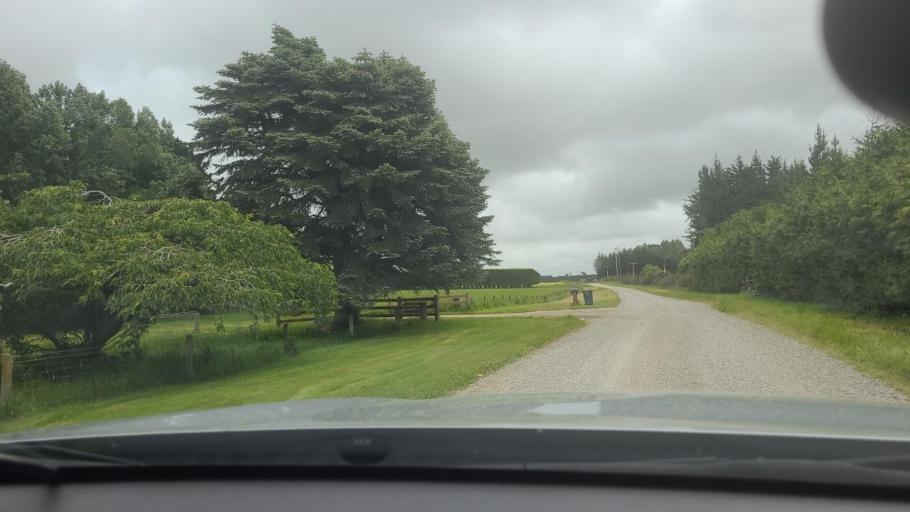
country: NZ
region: Southland
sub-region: Invercargill City
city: Invercargill
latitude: -46.3091
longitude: 168.3778
